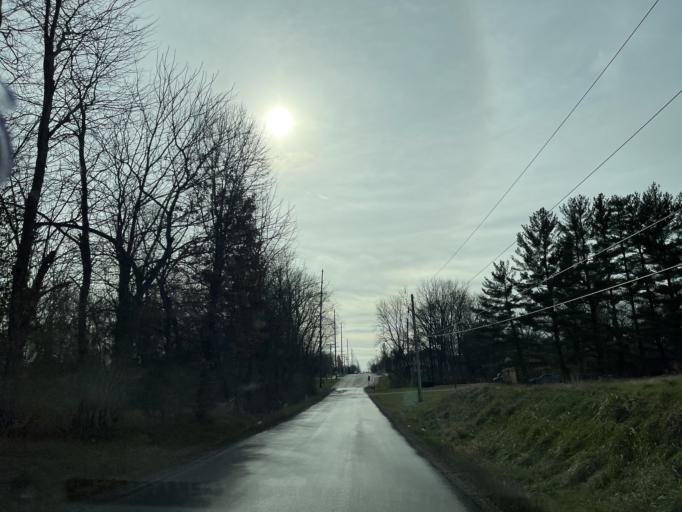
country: US
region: Illinois
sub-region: Sangamon County
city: Jerome
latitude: 39.7792
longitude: -89.7347
